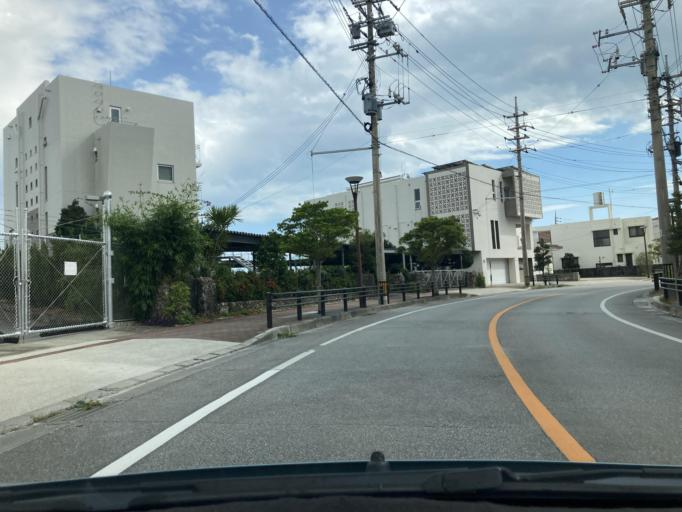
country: JP
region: Okinawa
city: Ginowan
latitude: 26.2535
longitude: 127.7756
